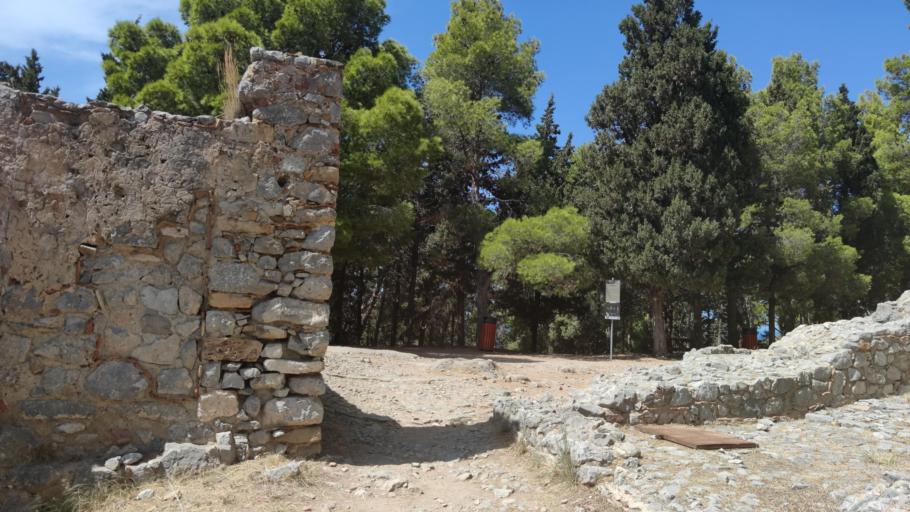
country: IT
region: Sicily
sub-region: Palermo
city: Cefalu
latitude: 38.0377
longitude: 14.0244
